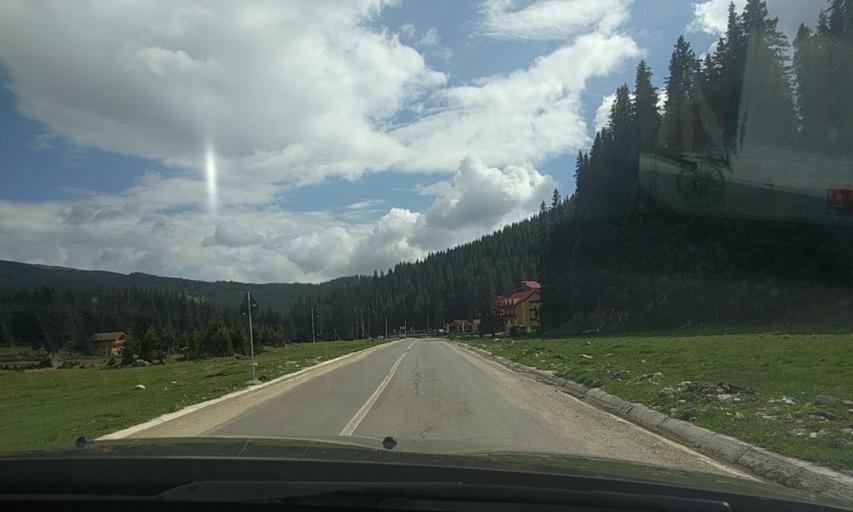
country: RO
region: Prahova
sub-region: Oras Busteni
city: Busteni
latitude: 45.3787
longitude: 25.4352
